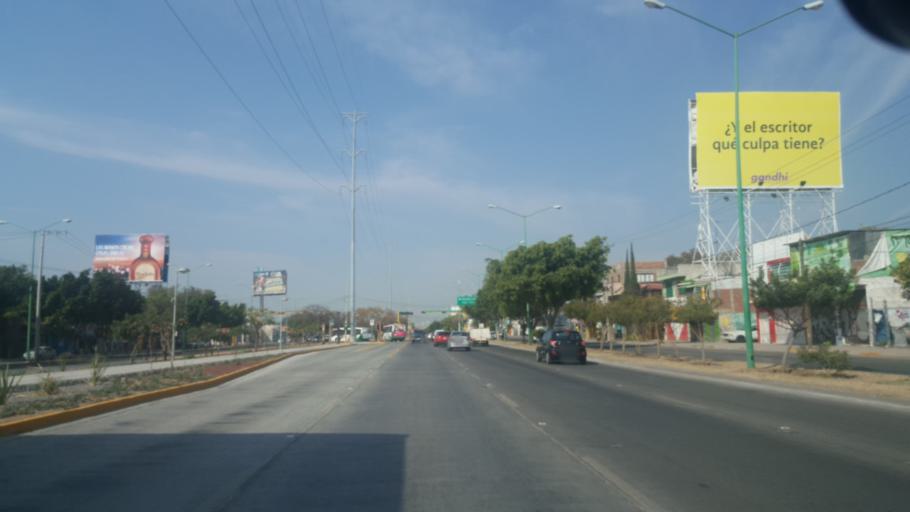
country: MX
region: Guanajuato
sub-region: Leon
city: Medina
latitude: 21.1424
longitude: -101.6361
